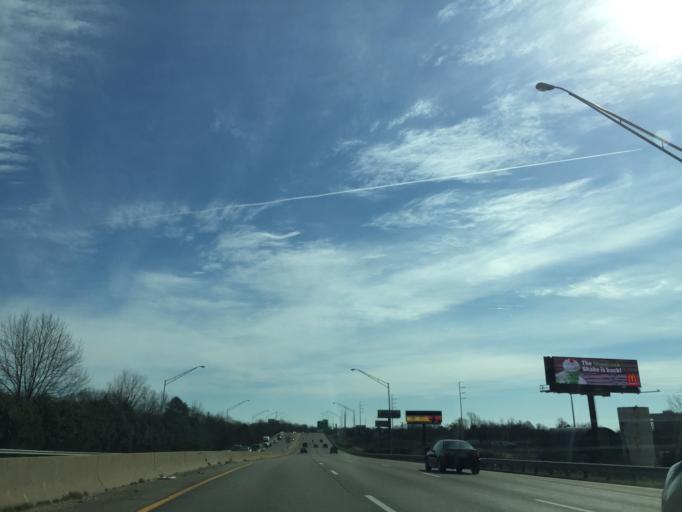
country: US
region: Virginia
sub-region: City of Hampton
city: Hampton
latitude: 37.0348
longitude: -76.3528
